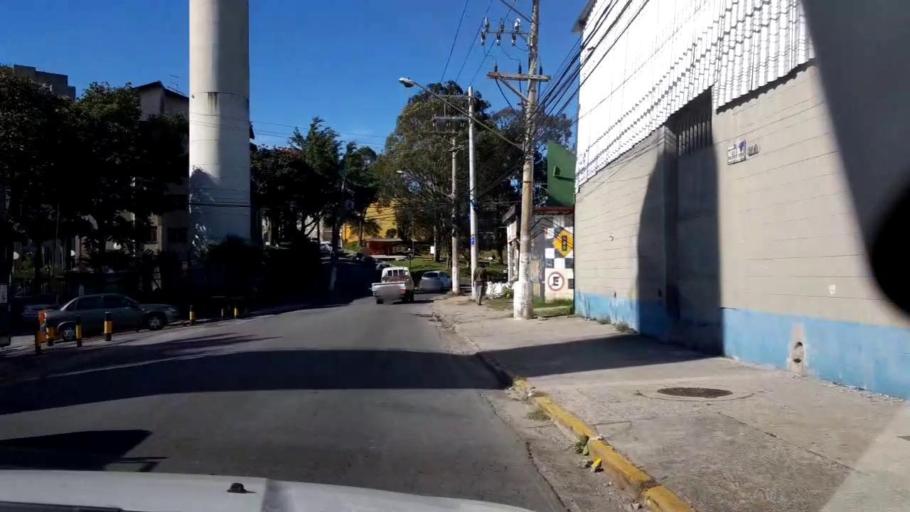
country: BR
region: Sao Paulo
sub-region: Ferraz De Vasconcelos
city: Ferraz de Vasconcelos
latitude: -23.5279
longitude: -46.3858
